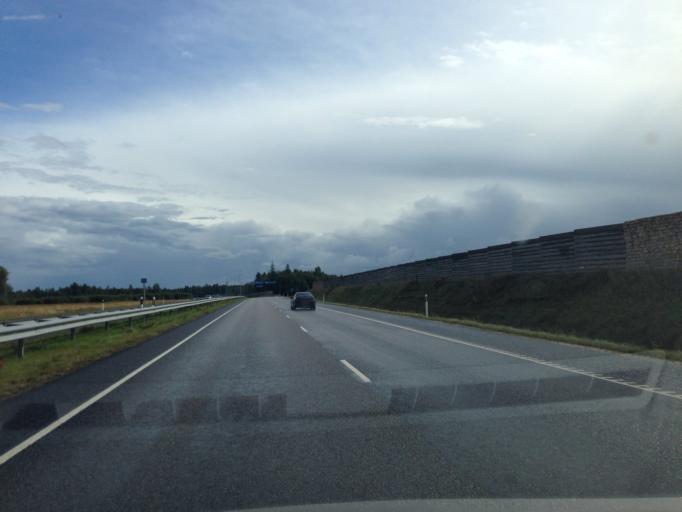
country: EE
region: Jaervamaa
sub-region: Paide linn
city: Paide
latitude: 58.9068
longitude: 25.6301
